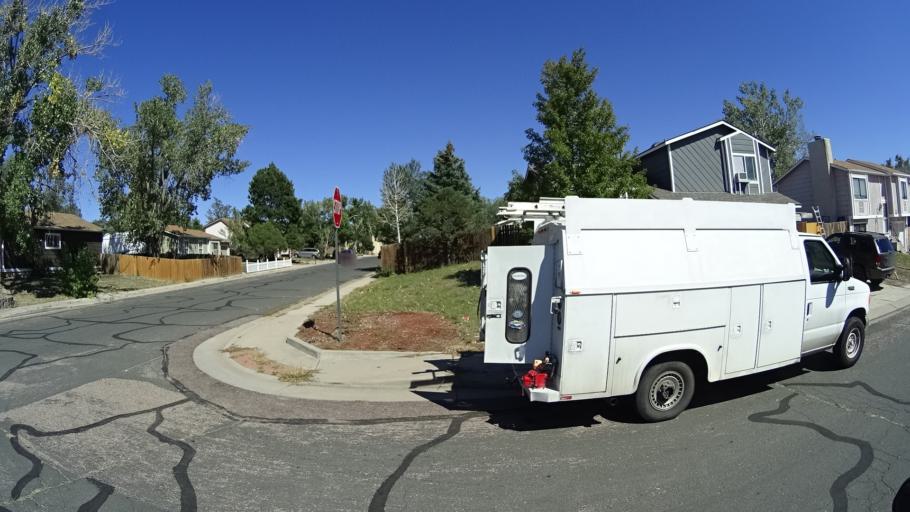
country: US
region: Colorado
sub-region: El Paso County
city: Stratmoor
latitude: 38.7838
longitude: -104.7423
